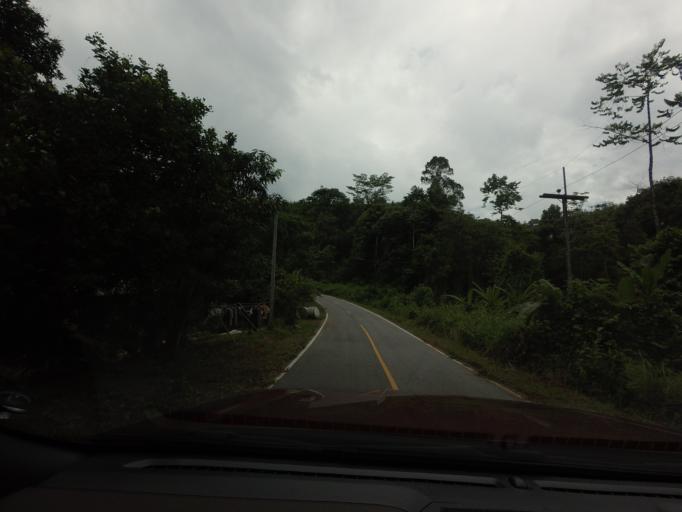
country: TH
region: Narathiwat
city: Sukhirin
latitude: 5.9854
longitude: 101.6816
